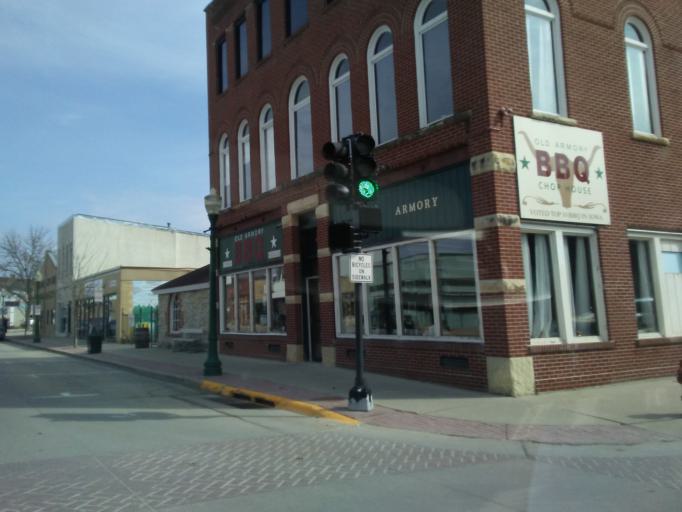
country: US
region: Iowa
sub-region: Winneshiek County
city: Decorah
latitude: 43.3041
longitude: -91.7910
